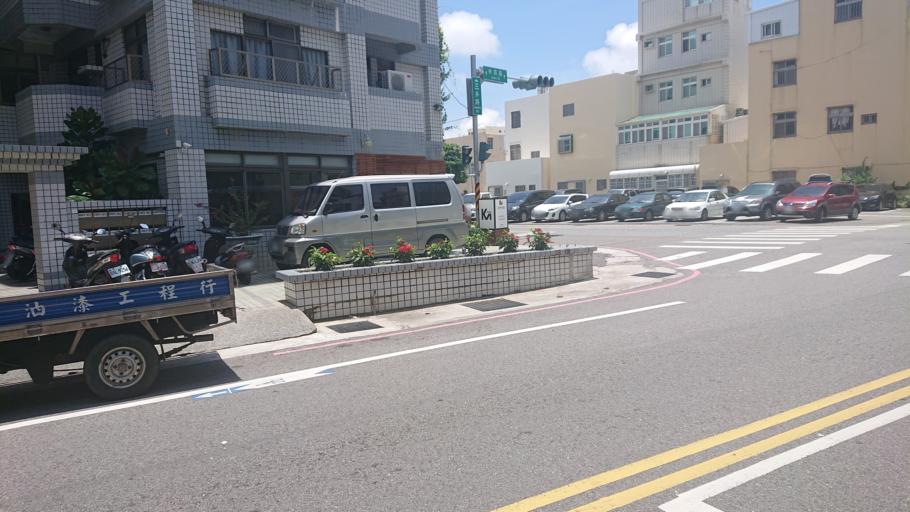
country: TW
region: Taiwan
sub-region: Penghu
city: Ma-kung
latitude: 23.5747
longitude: 119.5776
